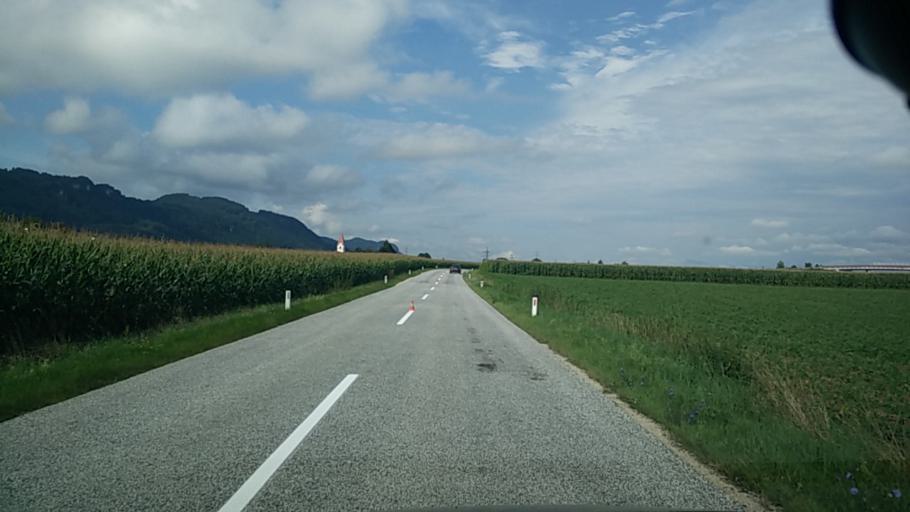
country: AT
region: Carinthia
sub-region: Politischer Bezirk Klagenfurt Land
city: Grafenstein
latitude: 46.6128
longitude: 14.4952
